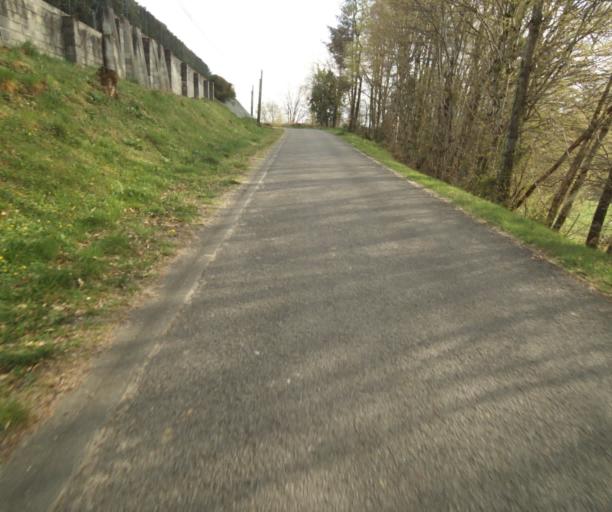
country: FR
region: Limousin
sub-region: Departement de la Correze
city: Naves
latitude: 45.3195
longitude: 1.7562
